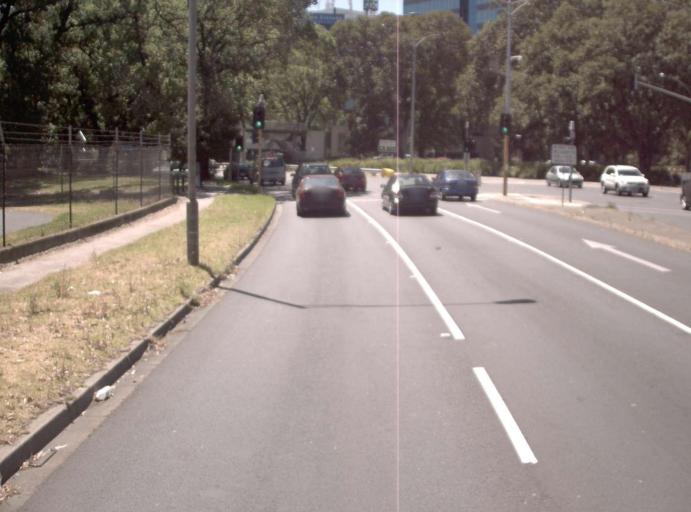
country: AU
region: Victoria
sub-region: Port Phillip
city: South Melbourne
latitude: -37.8368
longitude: 144.9732
